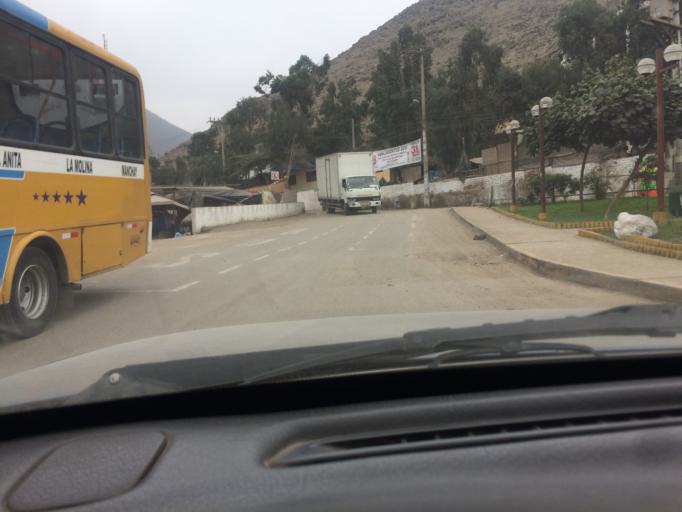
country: PE
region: Lima
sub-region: Lima
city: Cieneguilla
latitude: -12.1717
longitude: -76.8612
